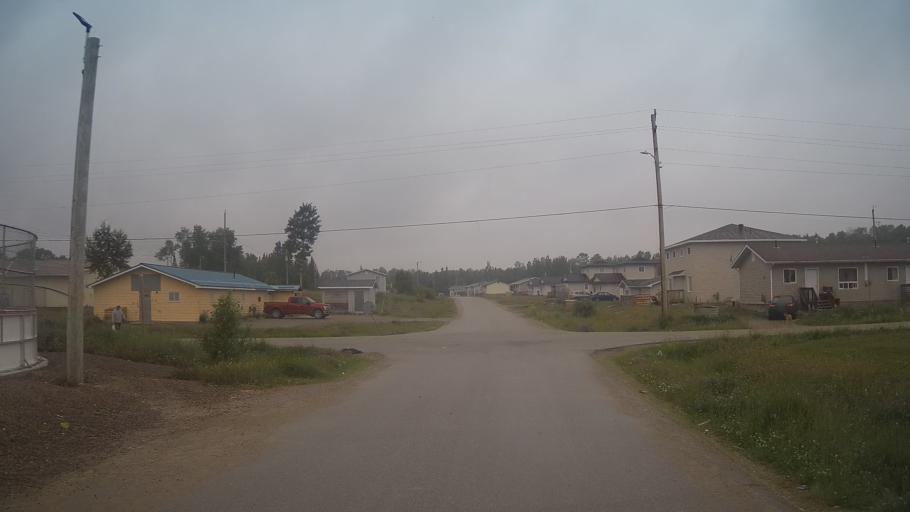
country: CA
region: Ontario
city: Greenstone
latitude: 49.7864
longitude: -86.5719
